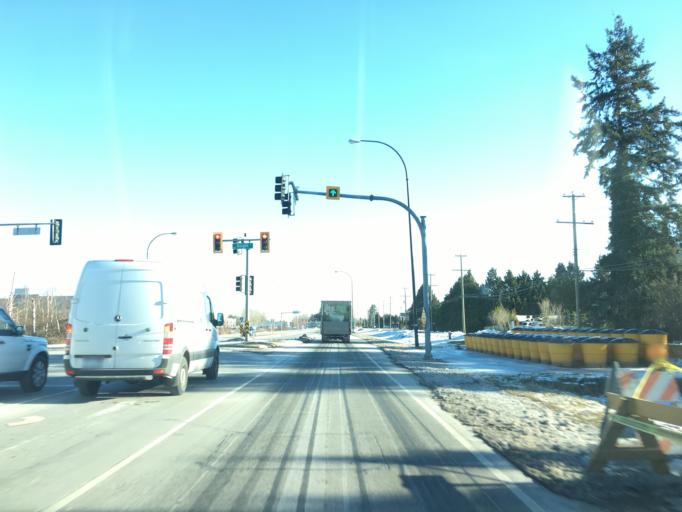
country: CA
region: British Columbia
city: Richmond
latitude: 49.1701
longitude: -123.0750
